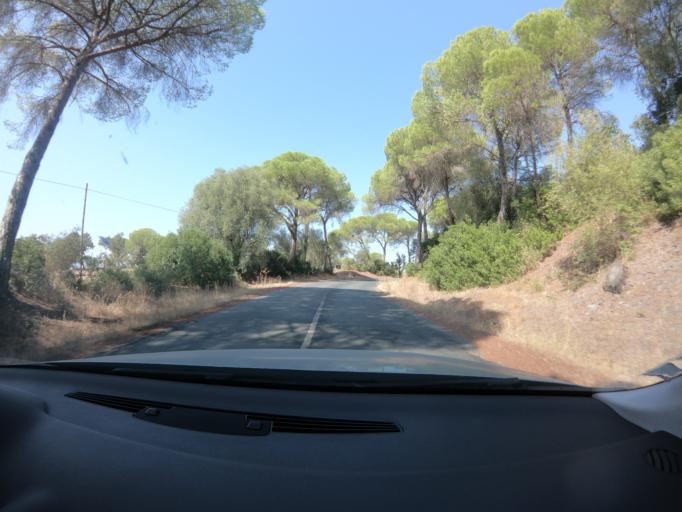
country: PT
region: Setubal
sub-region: Alcacer do Sal
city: Alcacer do Sal
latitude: 38.2949
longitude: -8.4051
